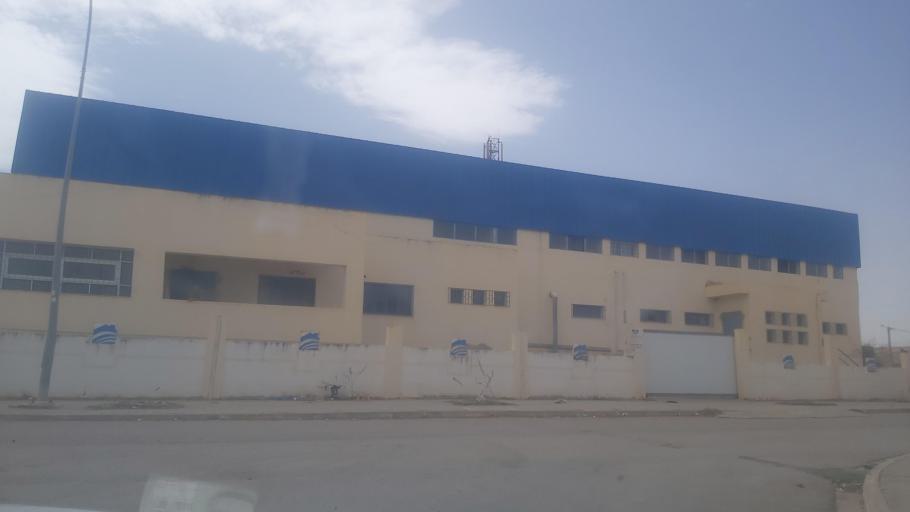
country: TN
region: Silyanah
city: Bu `Aradah
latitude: 36.3527
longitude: 9.6324
